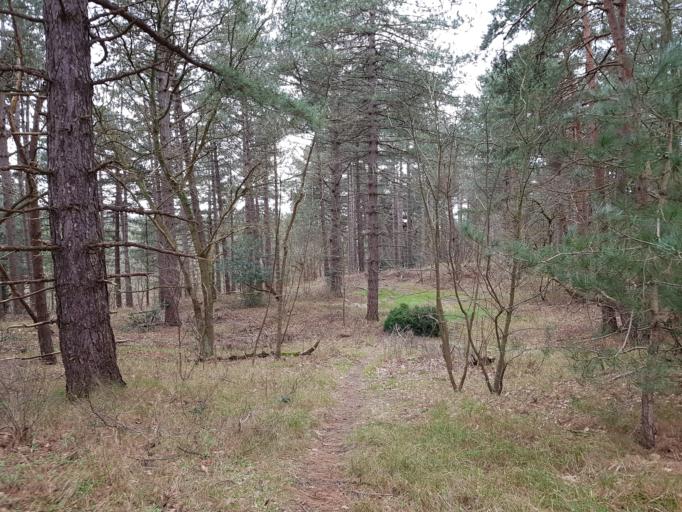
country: NL
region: North Holland
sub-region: Gemeente Bloemendaal
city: Bloemendaal
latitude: 52.3855
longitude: 4.5908
